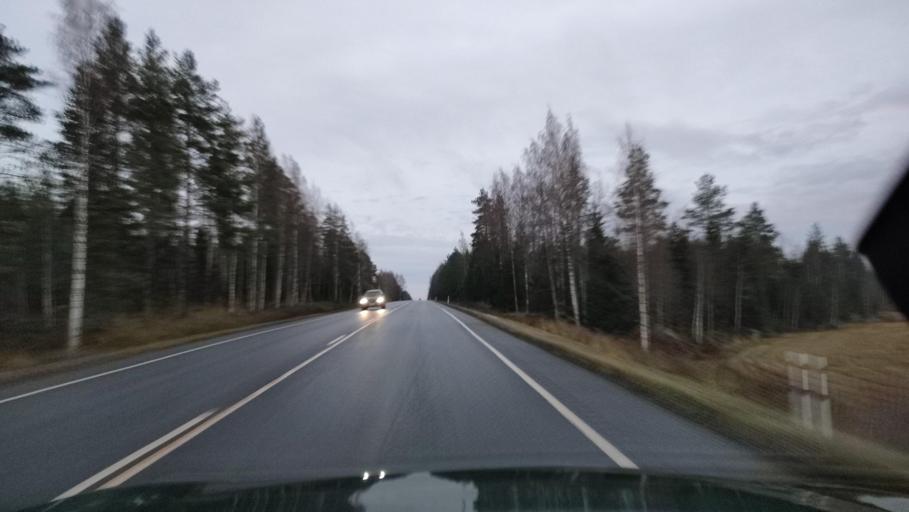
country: FI
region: Ostrobothnia
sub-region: Vaasa
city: Ristinummi
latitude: 63.0196
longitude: 21.7582
